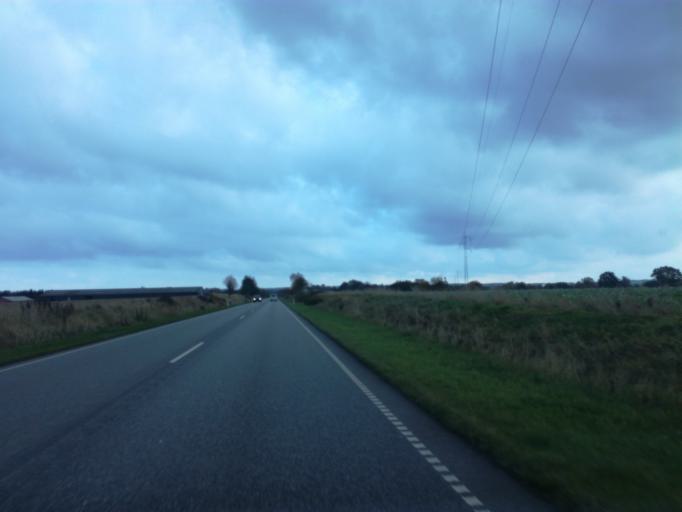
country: DK
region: South Denmark
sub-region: Vejle Kommune
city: Brejning
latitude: 55.6282
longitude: 9.7095
